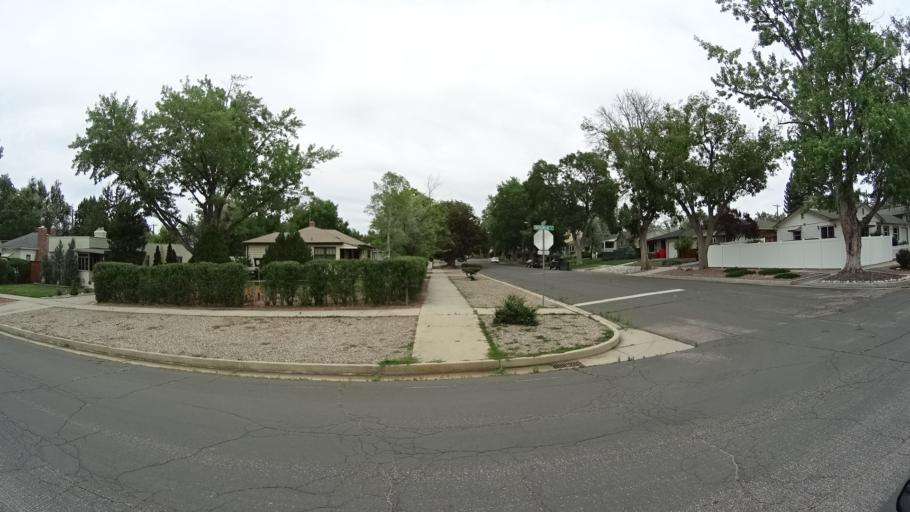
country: US
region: Colorado
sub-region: El Paso County
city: Colorado Springs
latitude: 38.8430
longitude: -104.7989
